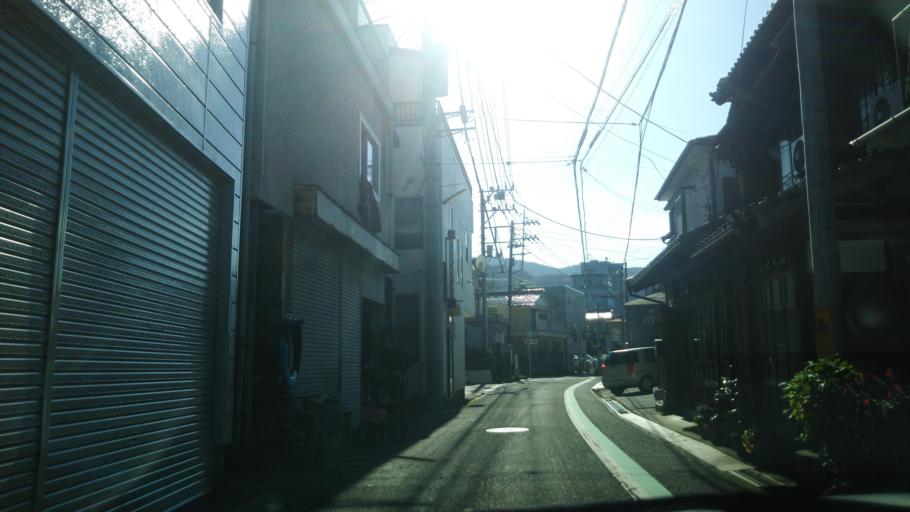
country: JP
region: Shizuoka
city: Numazu
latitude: 35.0231
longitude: 138.8991
